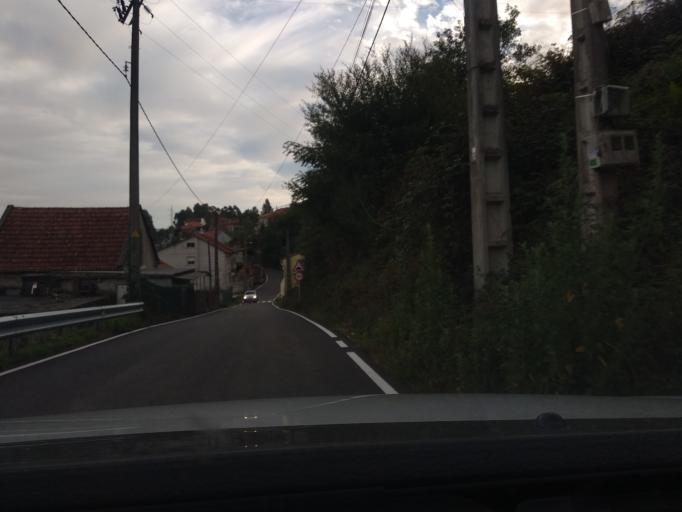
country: ES
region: Galicia
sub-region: Provincia de Pontevedra
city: Moana
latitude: 42.2940
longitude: -8.7385
